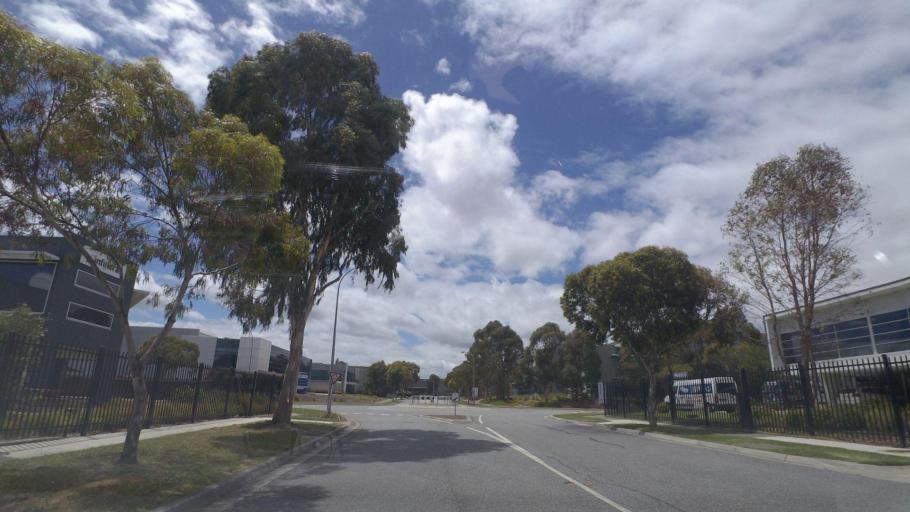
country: AU
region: Victoria
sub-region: Knox
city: Scoresby
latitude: -37.9061
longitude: 145.2421
